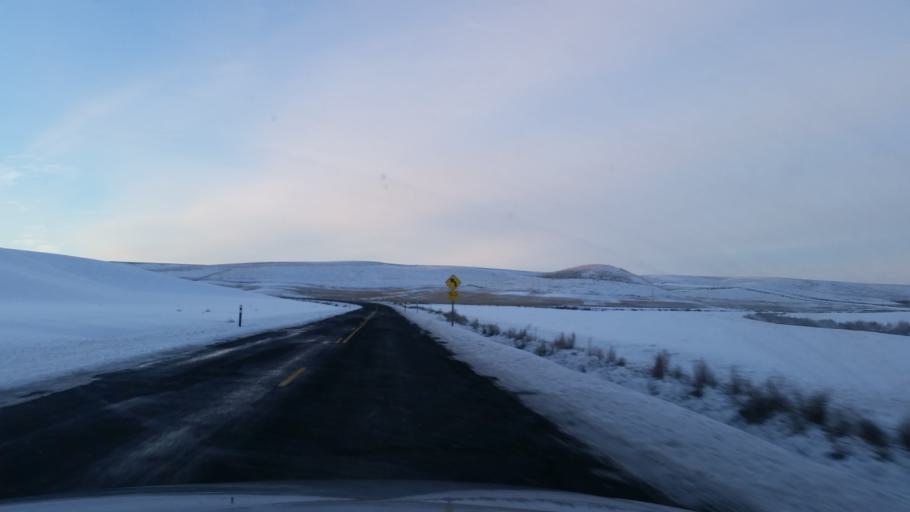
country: US
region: Washington
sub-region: Spokane County
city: Cheney
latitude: 47.1527
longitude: -117.8426
